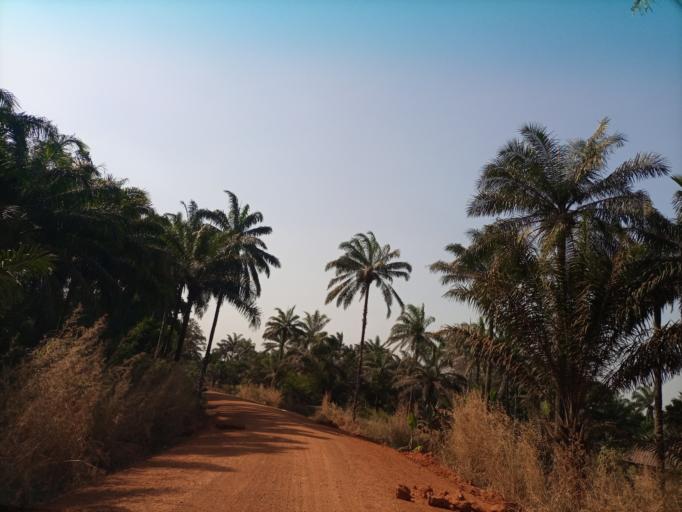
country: NG
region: Enugu
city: Aku
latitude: 6.7019
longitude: 7.3176
